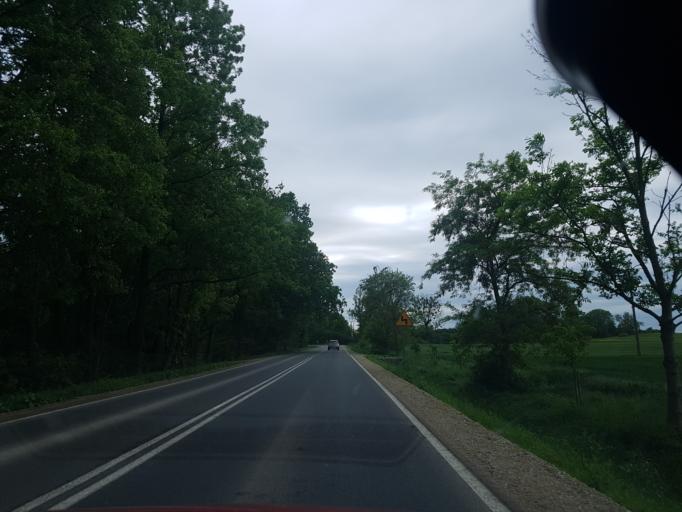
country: PL
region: Lower Silesian Voivodeship
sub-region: Powiat wroclawski
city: Katy Wroclawskie
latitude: 51.0161
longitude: 16.7522
